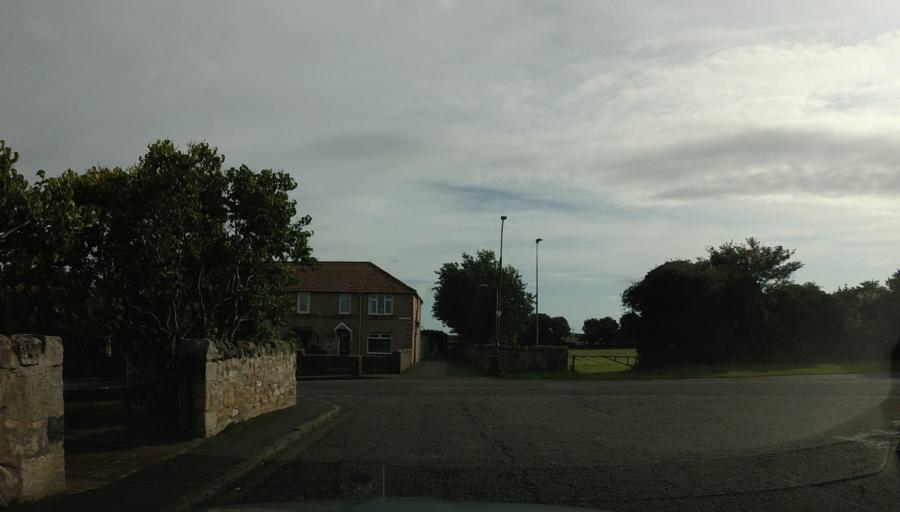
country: GB
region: Scotland
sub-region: East Lothian
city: Prestonpans
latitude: 55.9570
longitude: -2.9772
